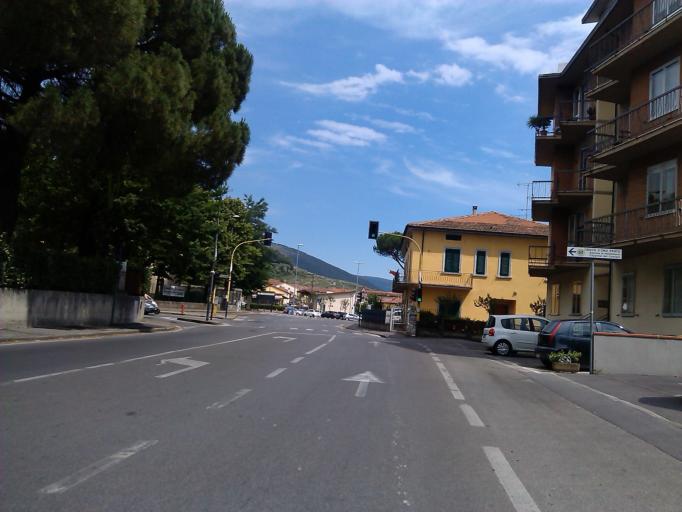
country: IT
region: Tuscany
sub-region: Provincia di Prato
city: Montemurlo
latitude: 43.9303
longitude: 11.0305
